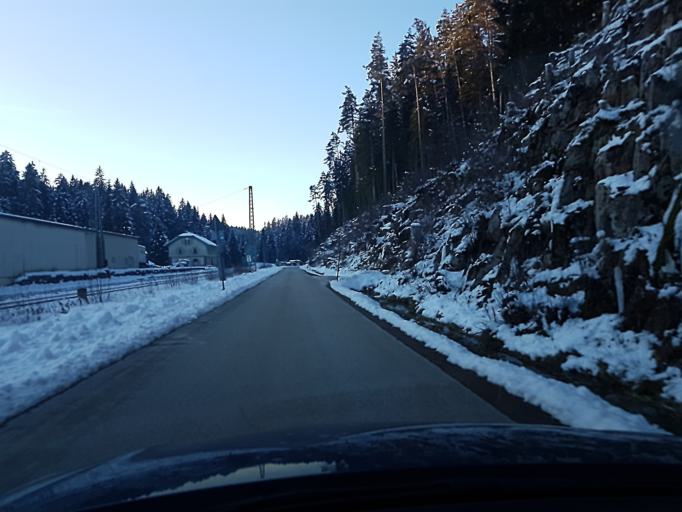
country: DE
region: Baden-Wuerttemberg
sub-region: Freiburg Region
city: Monchweiler
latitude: 48.0727
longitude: 8.4182
